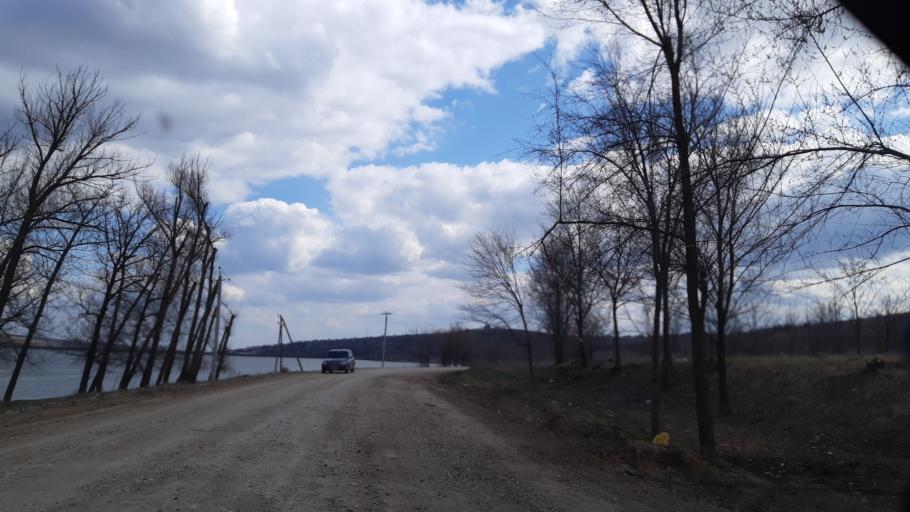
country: MD
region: Laloveni
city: Ialoveni
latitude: 46.8866
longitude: 28.7356
